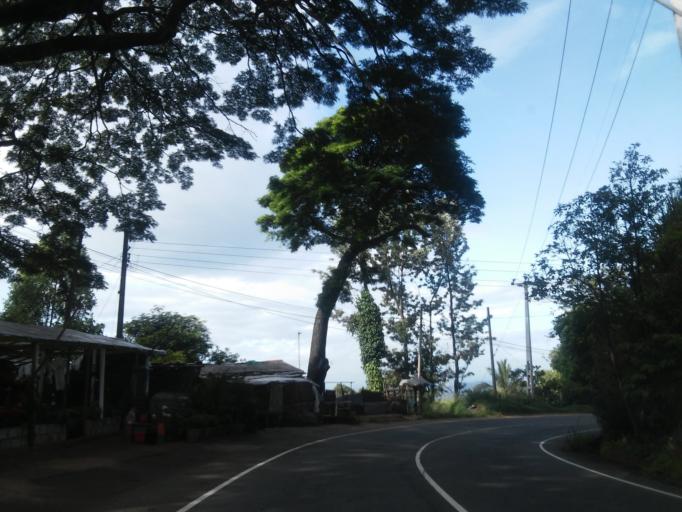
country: LK
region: Uva
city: Haputale
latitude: 6.7637
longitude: 80.9055
